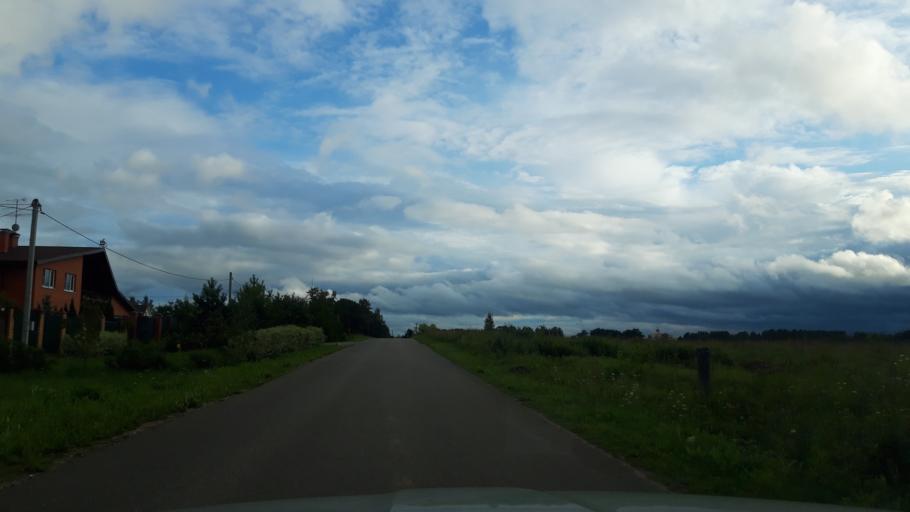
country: RU
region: Moskovskaya
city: Istra
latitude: 56.0974
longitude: 36.7987
